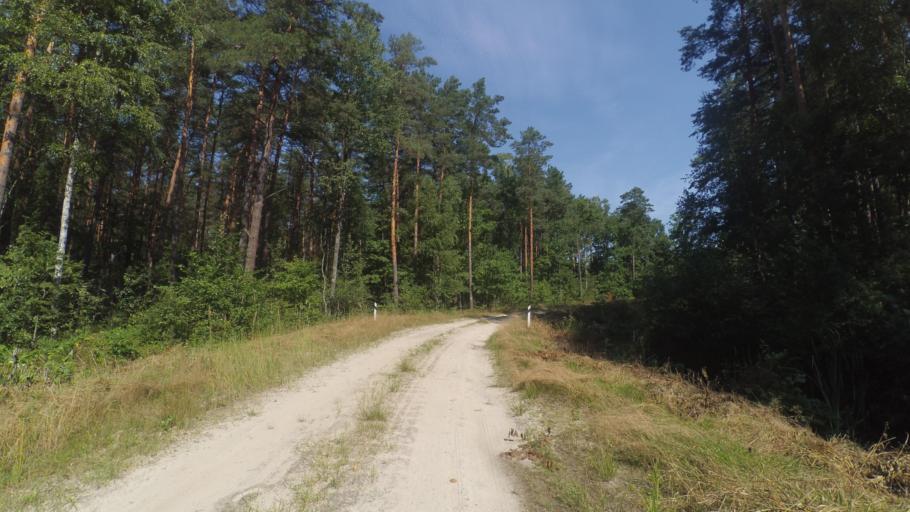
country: PL
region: Lublin Voivodeship
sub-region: Powiat wlodawski
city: Wlodawa
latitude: 51.6165
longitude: 23.6445
